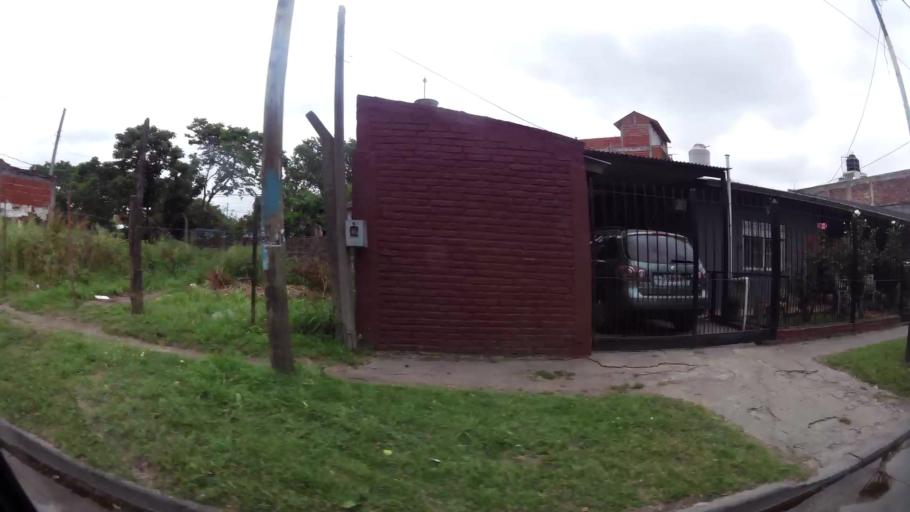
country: AR
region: Buenos Aires
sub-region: Partido de Ezeiza
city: Ezeiza
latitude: -34.8480
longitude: -58.5203
